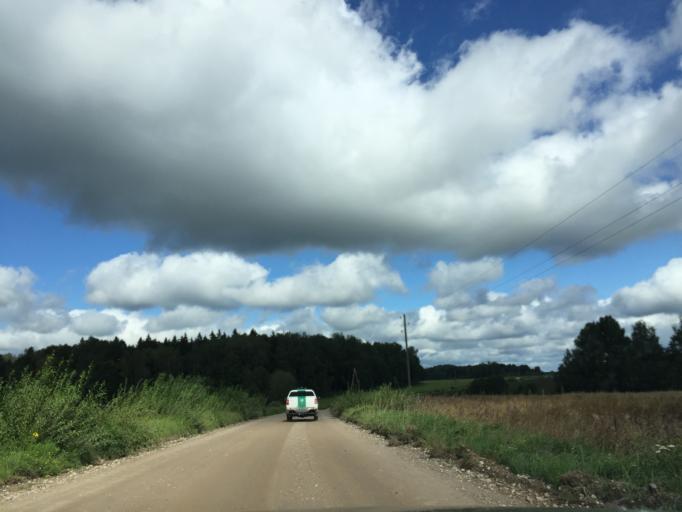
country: LV
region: Ligatne
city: Ligatne
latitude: 57.2157
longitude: 24.9488
